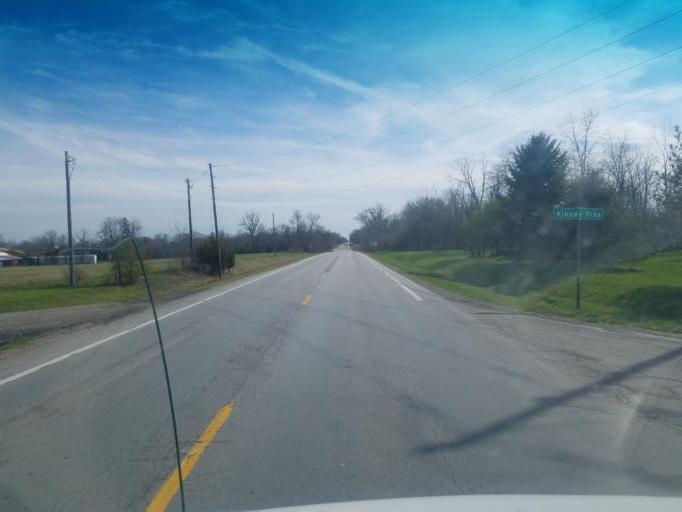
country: US
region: Ohio
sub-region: Union County
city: Richwood
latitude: 40.3508
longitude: -83.3021
